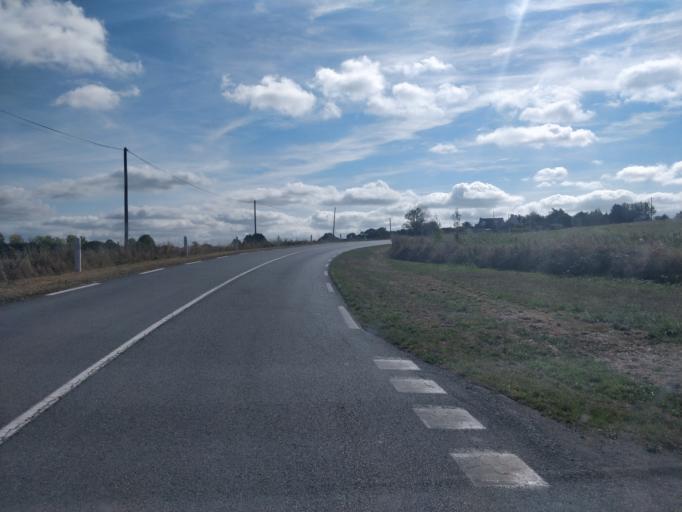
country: FR
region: Brittany
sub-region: Departement des Cotes-d'Armor
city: Erquy
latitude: 48.6144
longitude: -2.4707
